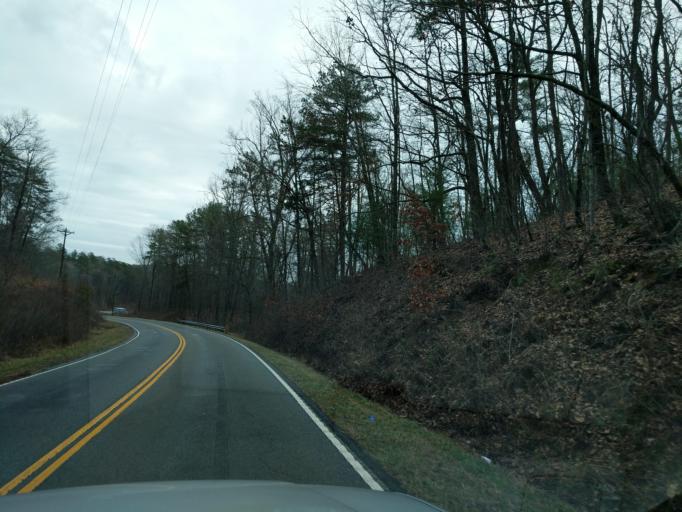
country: US
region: Georgia
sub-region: Rabun County
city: Clayton
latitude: 34.7669
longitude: -83.2539
